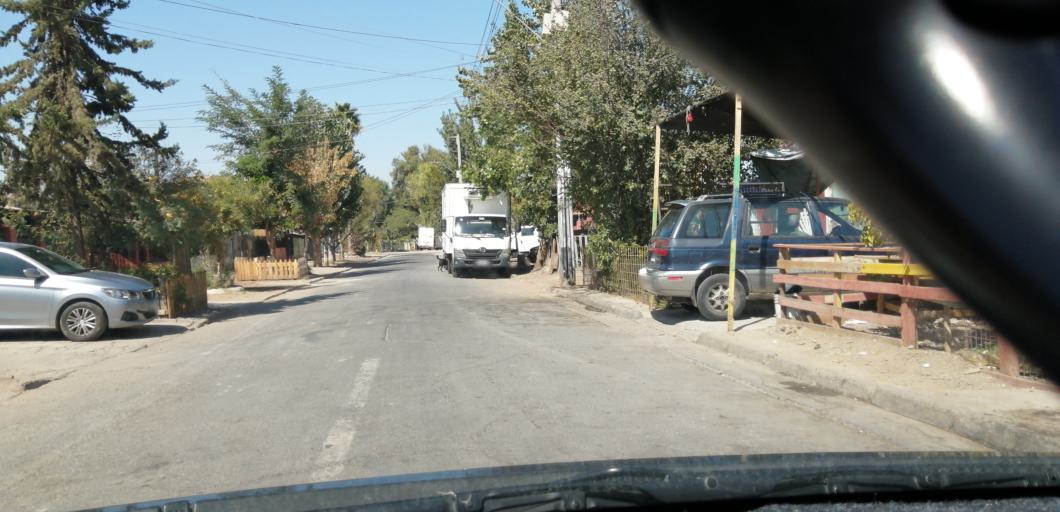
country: CL
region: Santiago Metropolitan
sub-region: Provincia de Santiago
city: Lo Prado
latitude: -33.4380
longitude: -70.7434
